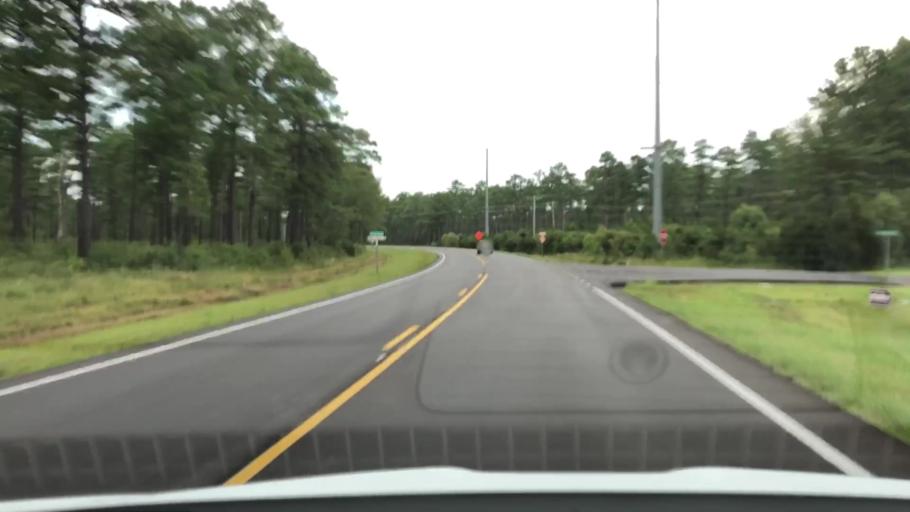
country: US
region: North Carolina
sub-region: Onslow County
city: Swansboro
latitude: 34.8076
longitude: -77.1343
